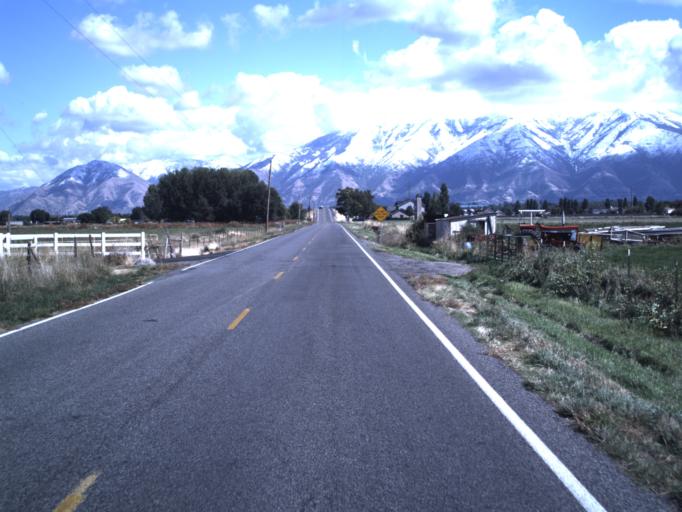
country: US
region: Utah
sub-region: Utah County
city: Spanish Fork
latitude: 40.1155
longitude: -111.6777
